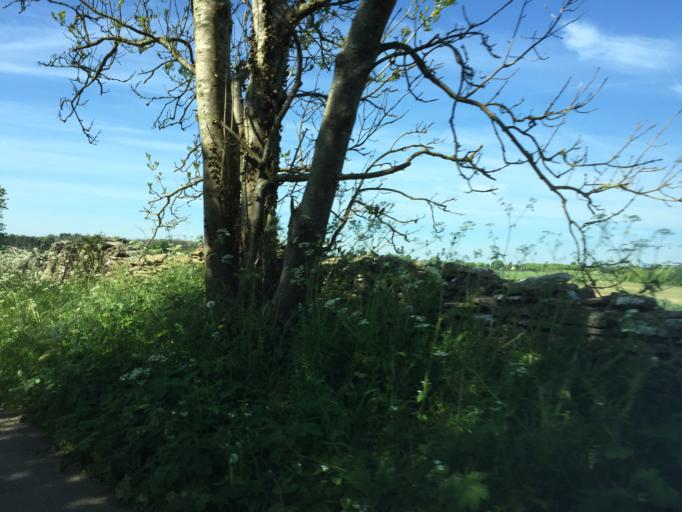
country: GB
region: England
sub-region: Wiltshire
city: Luckington
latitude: 51.6106
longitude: -2.2597
